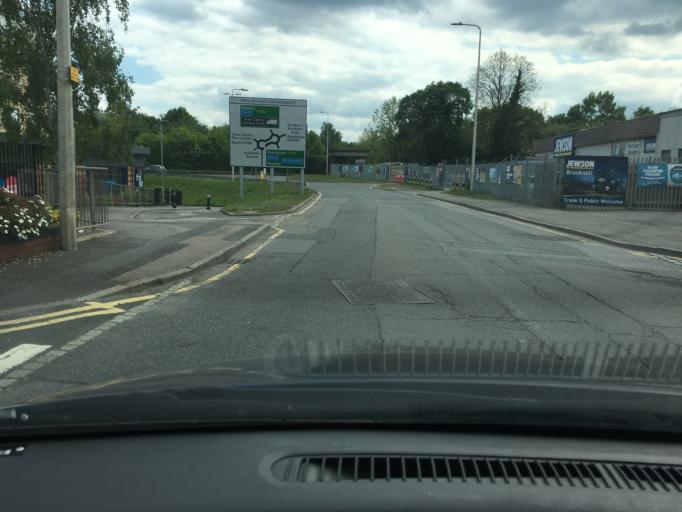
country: GB
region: England
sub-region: Bracknell Forest
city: Bracknell
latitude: 51.4148
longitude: -0.7617
